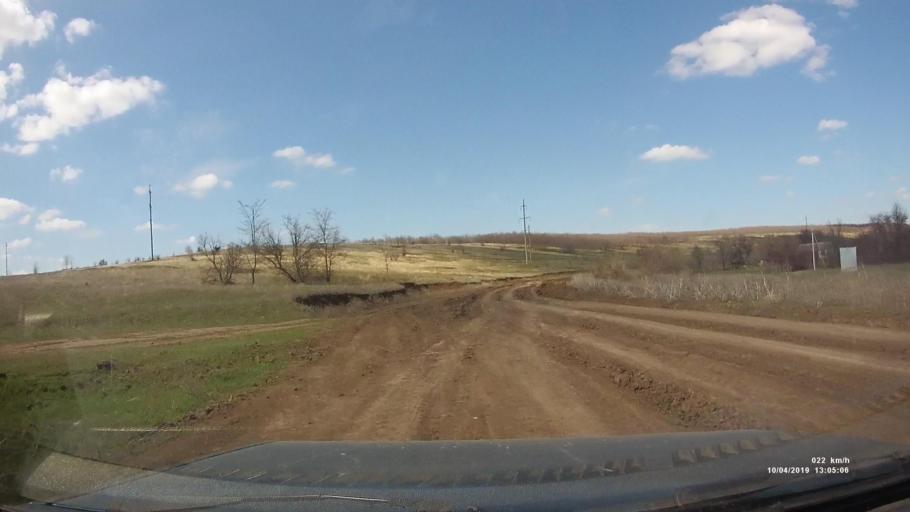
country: RU
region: Rostov
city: Masalovka
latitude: 48.3869
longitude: 40.2336
